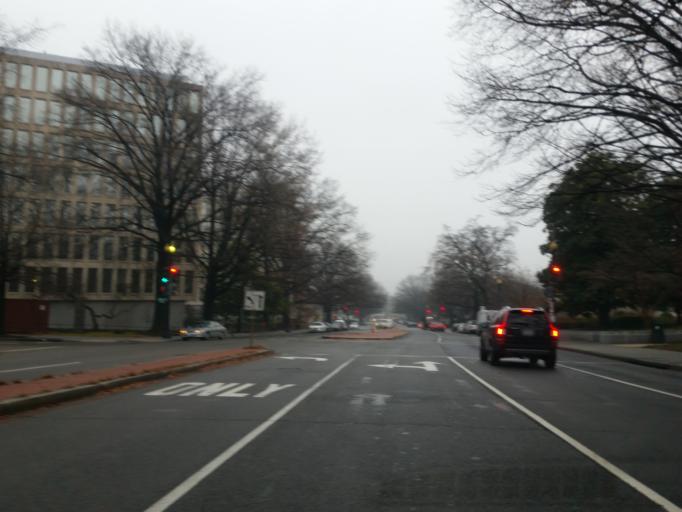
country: US
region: Washington, D.C.
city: Washington, D.C.
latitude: 38.8947
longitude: -77.0456
